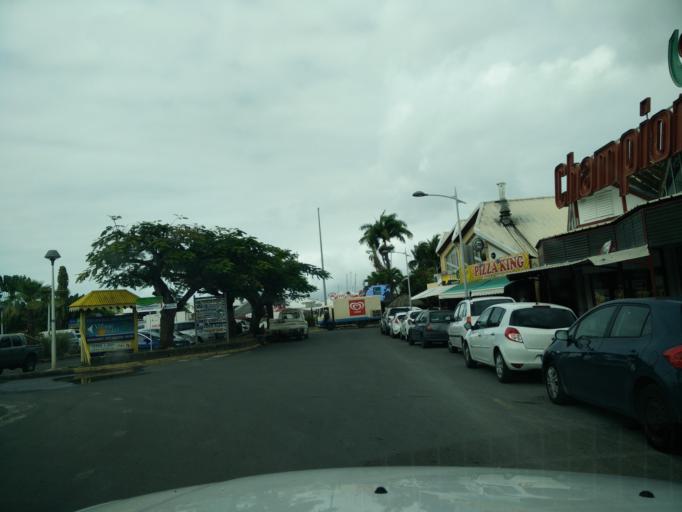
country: GP
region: Guadeloupe
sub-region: Guadeloupe
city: Pointe-a-Pitre
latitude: 16.2206
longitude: -61.5274
